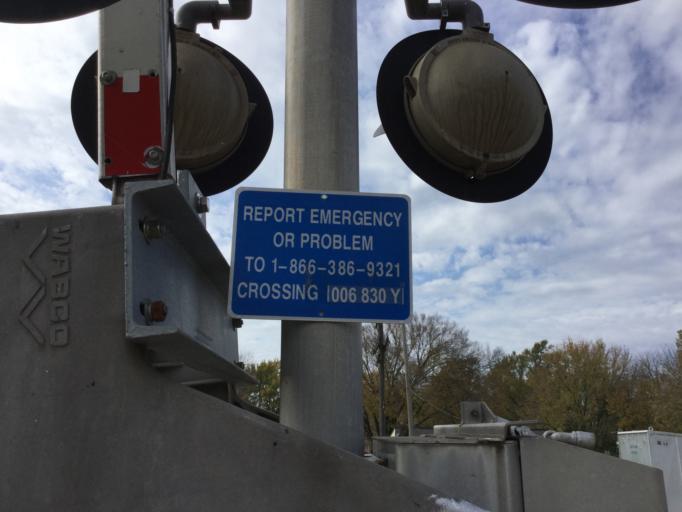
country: US
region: Kansas
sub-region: Montgomery County
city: Cherryvale
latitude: 37.2656
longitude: -95.5521
